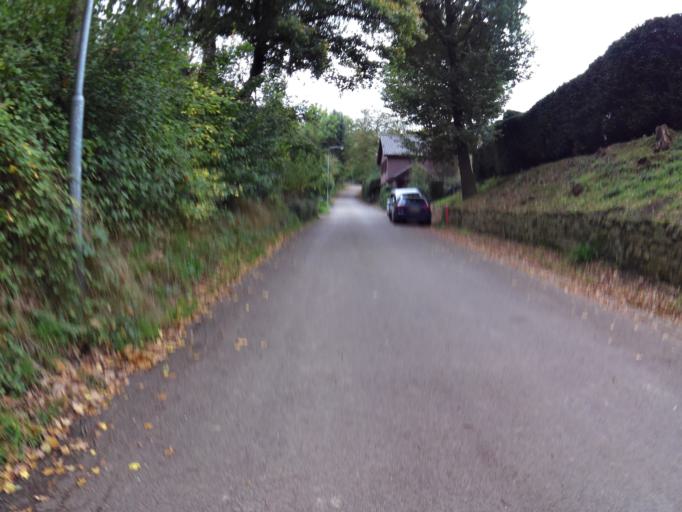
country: NL
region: Limburg
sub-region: Gemeente Voerendaal
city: Kunrade
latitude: 50.8721
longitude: 5.9463
